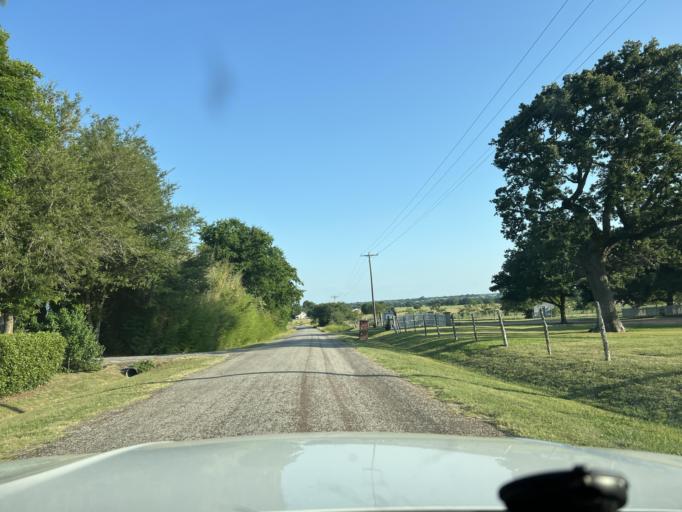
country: US
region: Texas
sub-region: Washington County
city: Brenham
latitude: 30.2245
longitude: -96.3796
